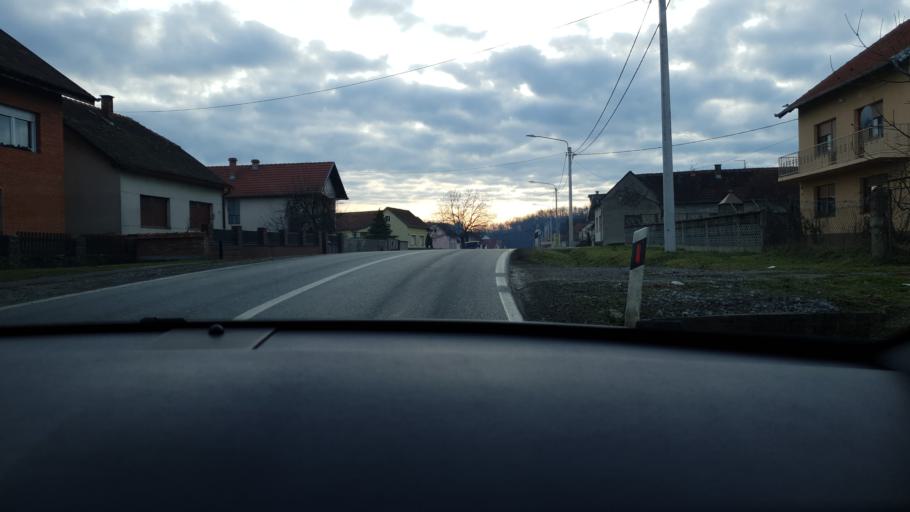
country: HR
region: Pozesko-Slavonska
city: Vidovci
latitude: 45.3537
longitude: 17.7254
